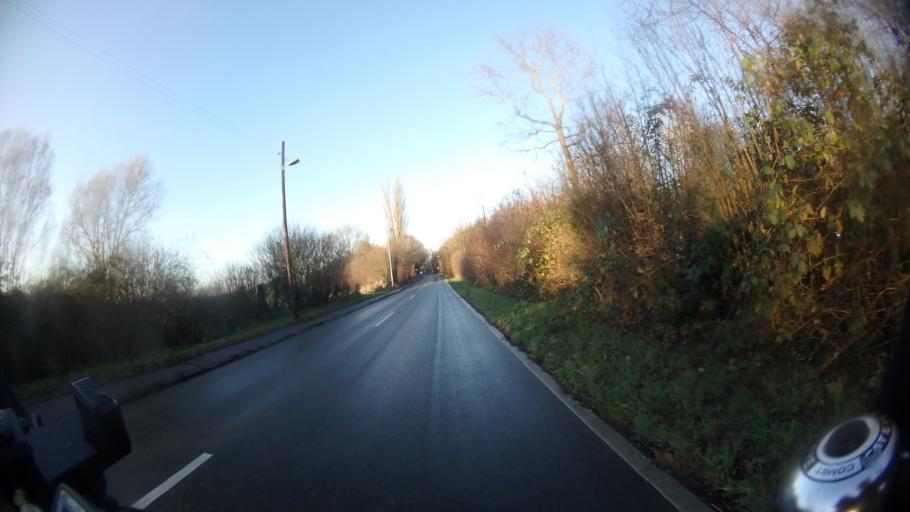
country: DE
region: Schleswig-Holstein
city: Travemuende
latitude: 53.9817
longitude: 10.8636
